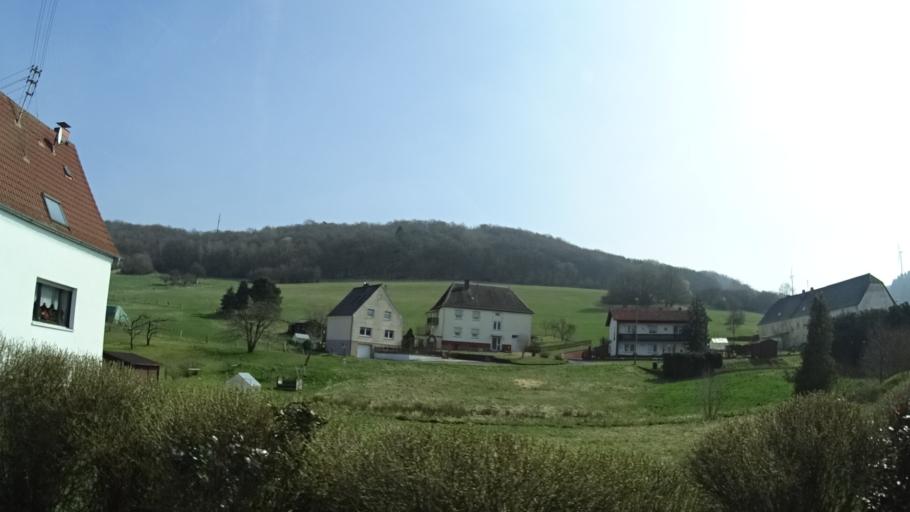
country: DE
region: Rheinland-Pfalz
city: Hoppstadten-Weiersbach
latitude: 49.6062
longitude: 7.1948
